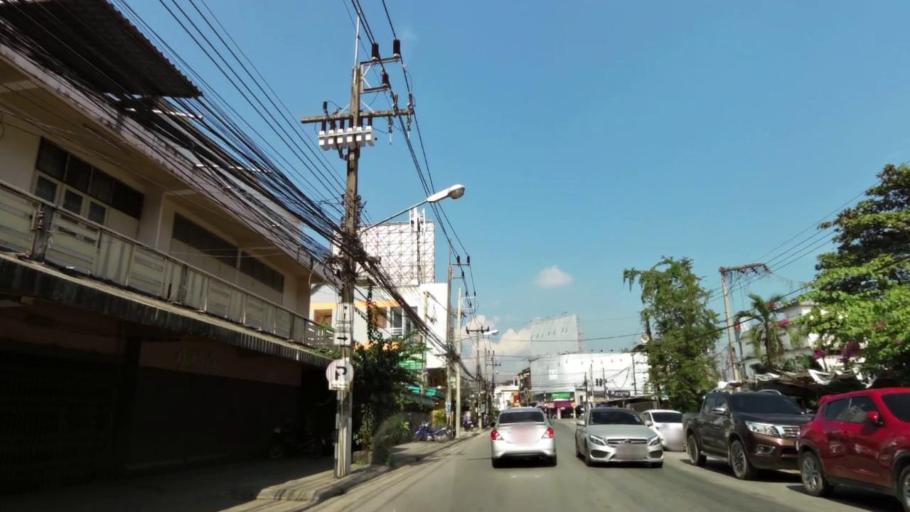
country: TH
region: Chiang Rai
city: Chiang Rai
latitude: 19.9061
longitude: 99.8286
